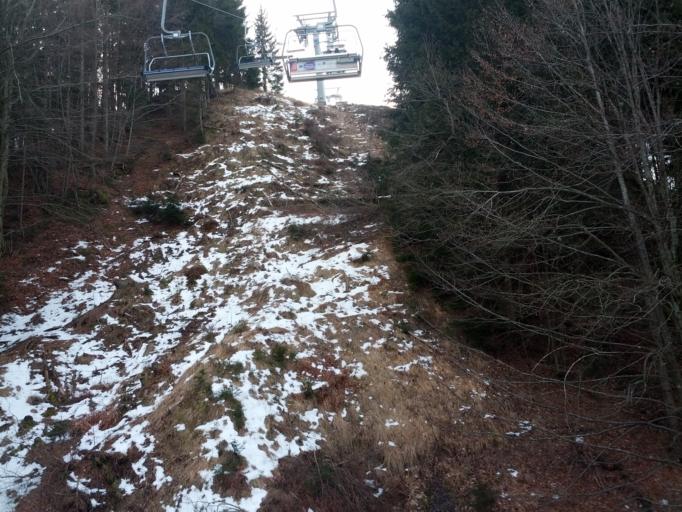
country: SI
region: Kranjska Gora
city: Kranjska Gora
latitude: 46.4842
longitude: 13.7635
